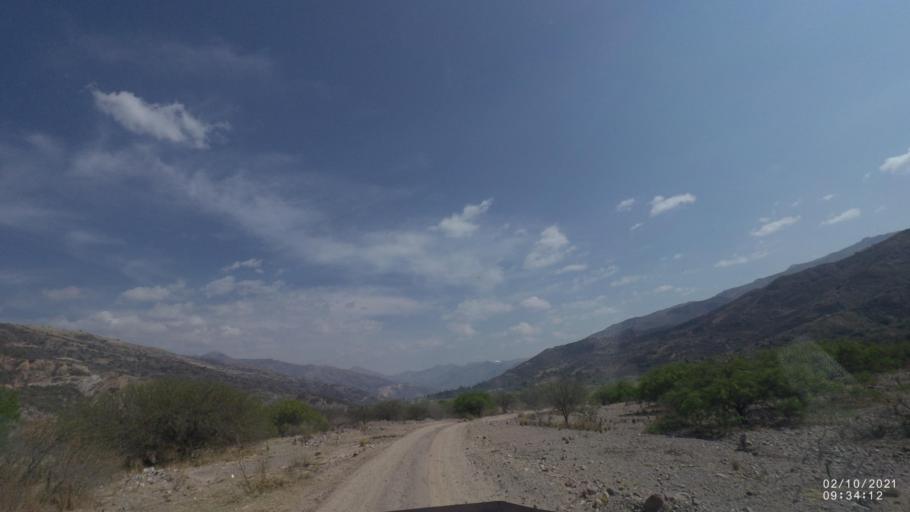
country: BO
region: Cochabamba
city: Irpa Irpa
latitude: -17.8408
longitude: -66.3194
